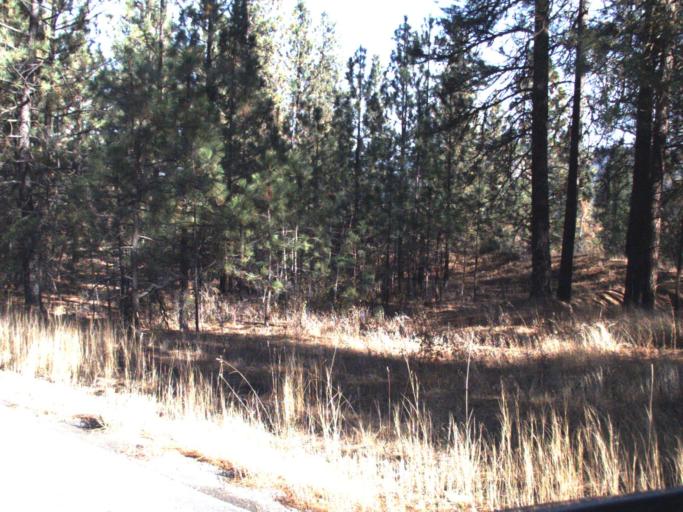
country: US
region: Washington
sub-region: Stevens County
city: Kettle Falls
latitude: 48.5908
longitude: -118.1476
